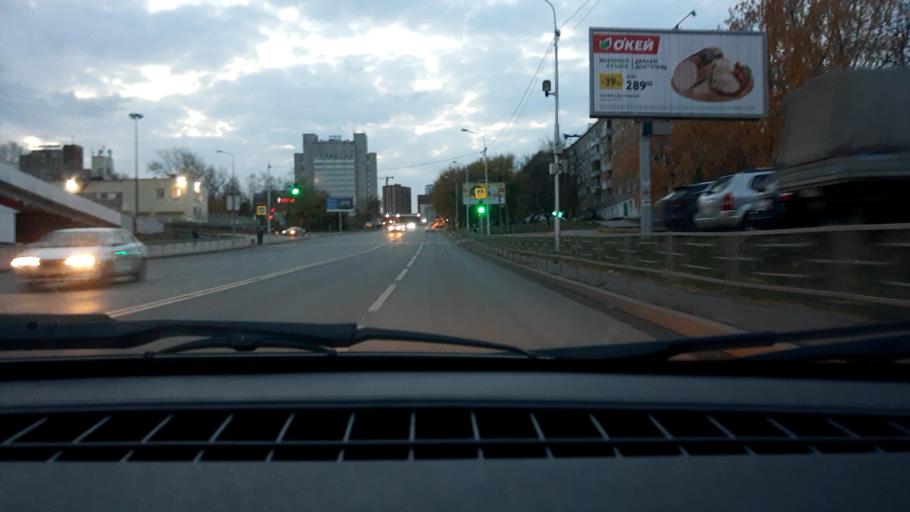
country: RU
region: Bashkortostan
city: Ufa
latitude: 54.7197
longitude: 56.0013
